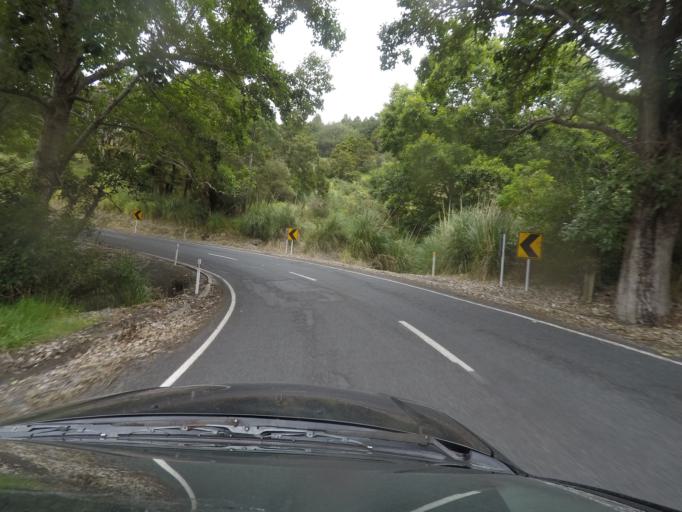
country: NZ
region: Auckland
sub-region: Auckland
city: Warkworth
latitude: -36.2735
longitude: 174.6964
